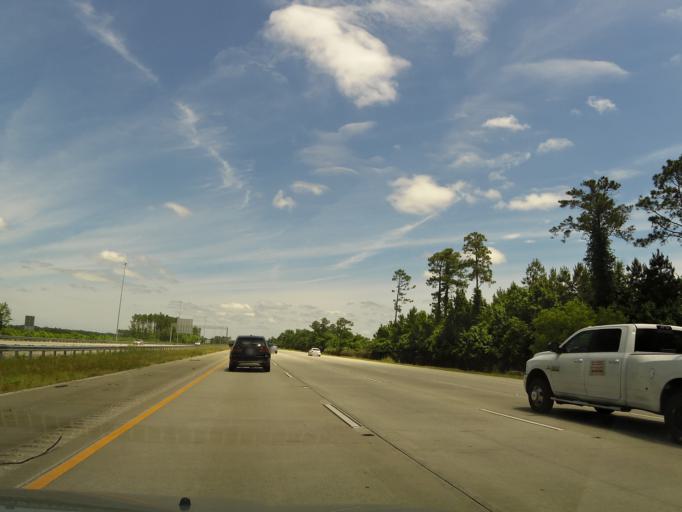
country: US
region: Georgia
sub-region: Glynn County
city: Country Club Estates
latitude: 31.2672
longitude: -81.4928
